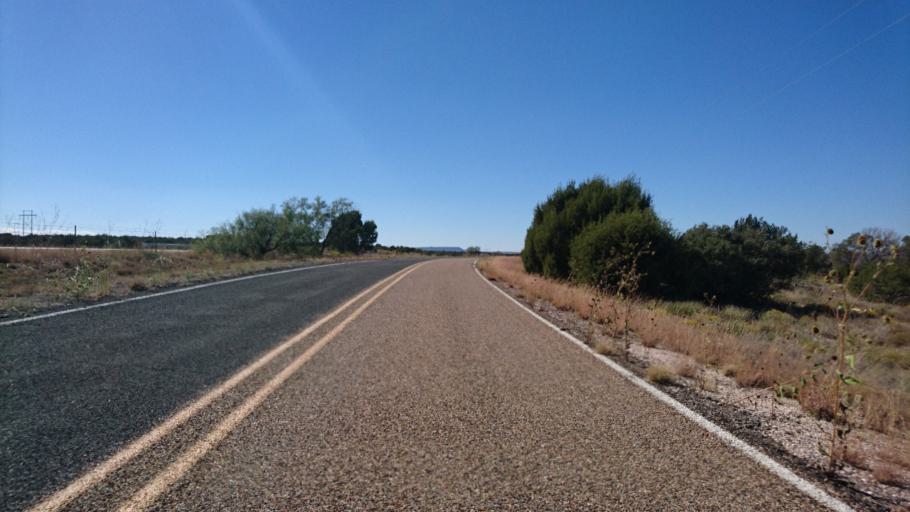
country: US
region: New Mexico
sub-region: Quay County
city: Tucumcari
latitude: 35.0668
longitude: -104.1842
